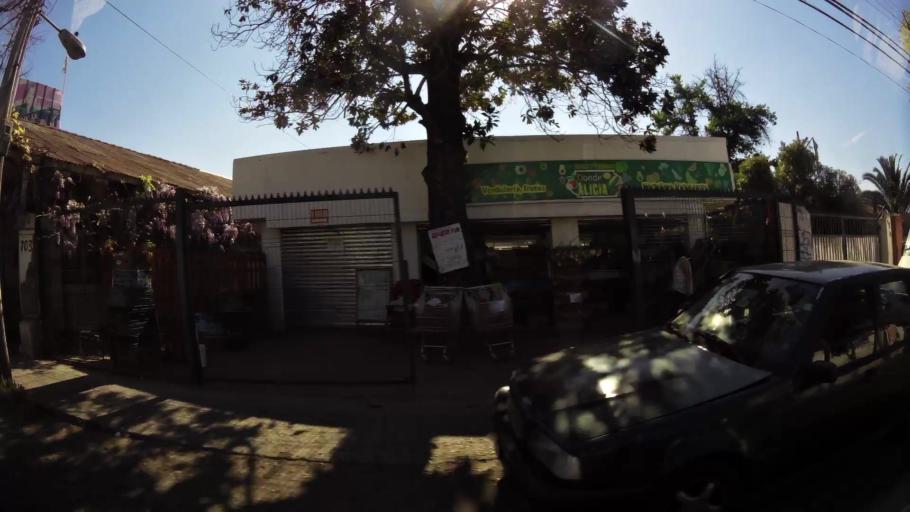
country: CL
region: Santiago Metropolitan
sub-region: Provincia de Talagante
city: Penaflor
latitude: -33.6058
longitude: -70.8961
